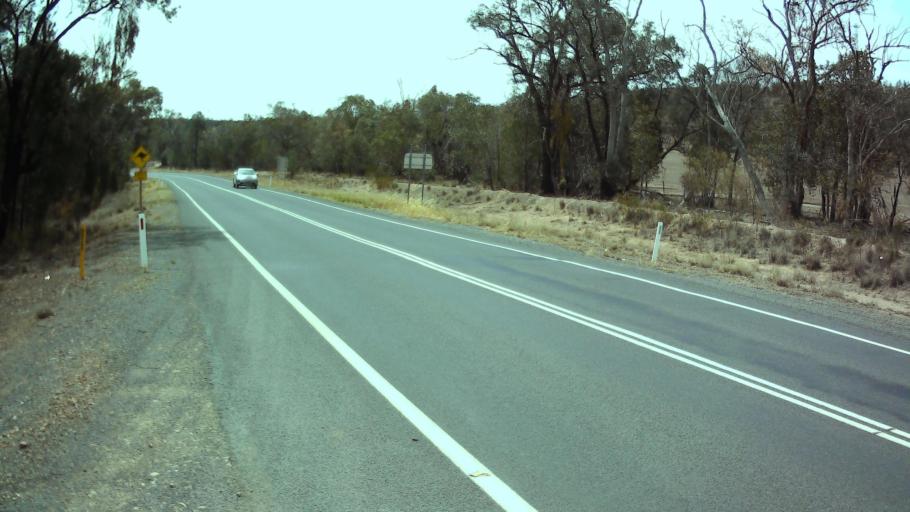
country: AU
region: New South Wales
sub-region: Weddin
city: Grenfell
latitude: -33.8847
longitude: 148.1398
